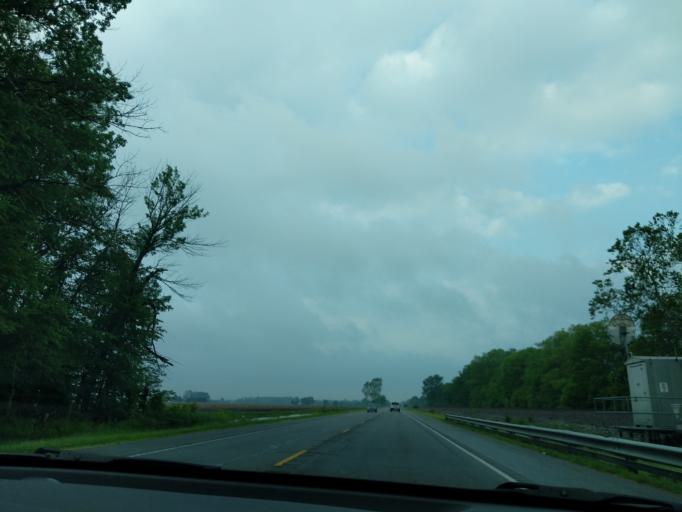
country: US
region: Indiana
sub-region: Hancock County
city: Fortville
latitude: 39.9215
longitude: -85.8715
